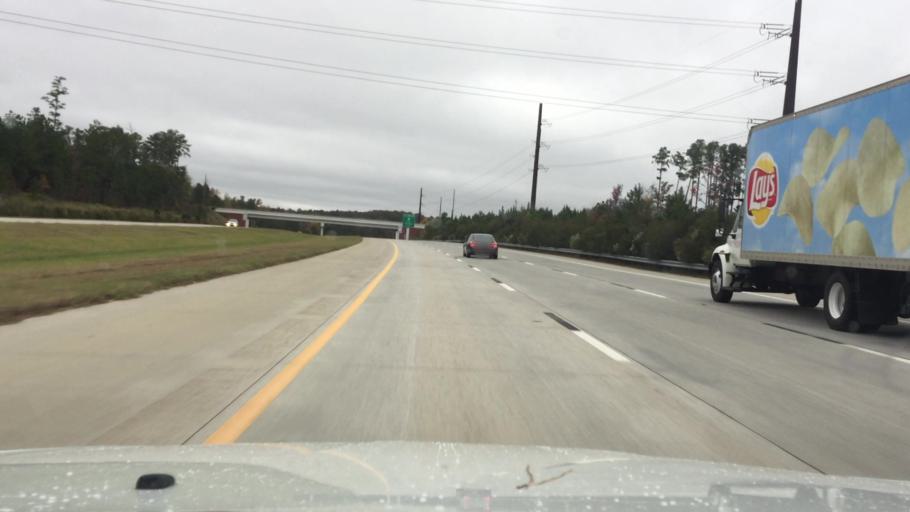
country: US
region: North Carolina
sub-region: Wake County
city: Green Level
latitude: 35.8195
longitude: -78.8923
